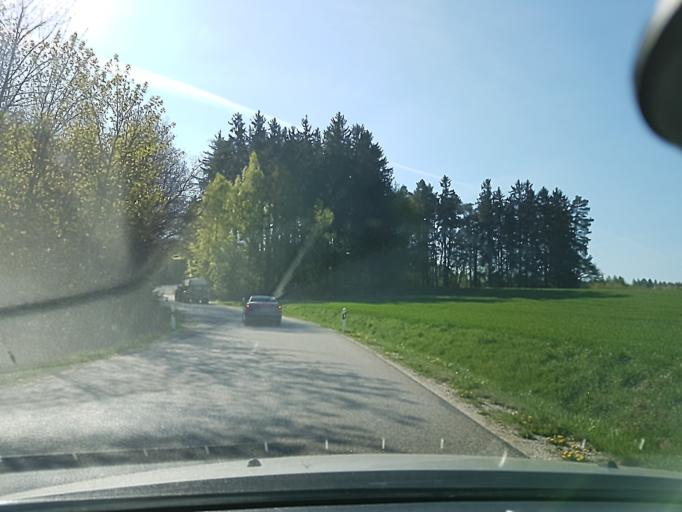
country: DE
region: Bavaria
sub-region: Lower Bavaria
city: Furth
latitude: 48.3990
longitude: 12.4010
